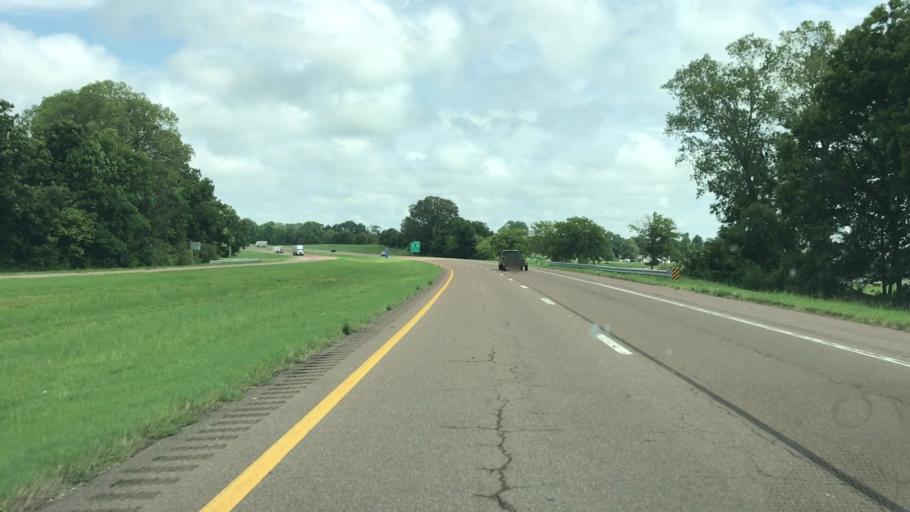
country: US
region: Tennessee
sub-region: Dyer County
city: Dyersburg
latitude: 36.0675
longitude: -89.3615
